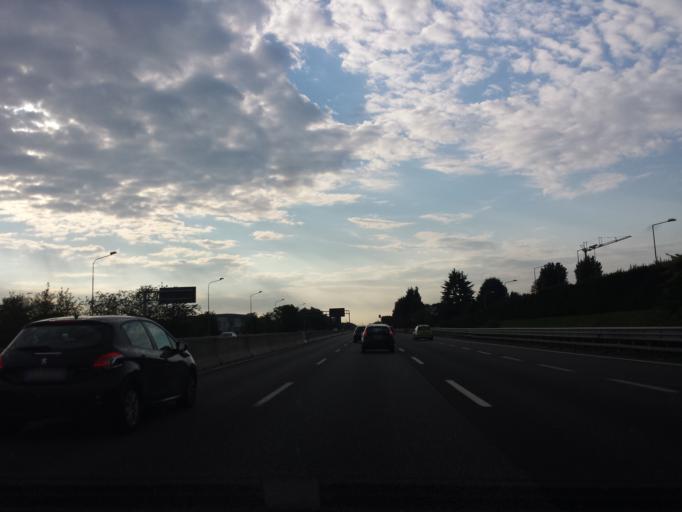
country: IT
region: Lombardy
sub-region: Citta metropolitana di Milano
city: Cerro Maggiore
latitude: 45.6015
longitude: 8.9488
